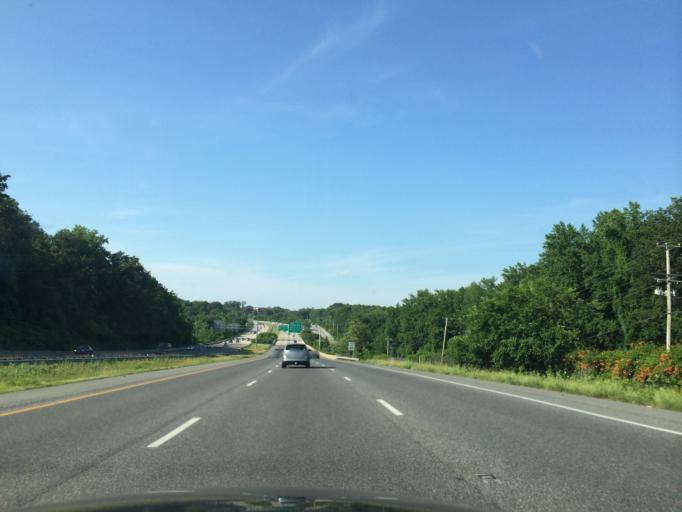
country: US
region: Maryland
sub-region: Anne Arundel County
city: Gambrills
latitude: 39.0777
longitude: -76.6281
